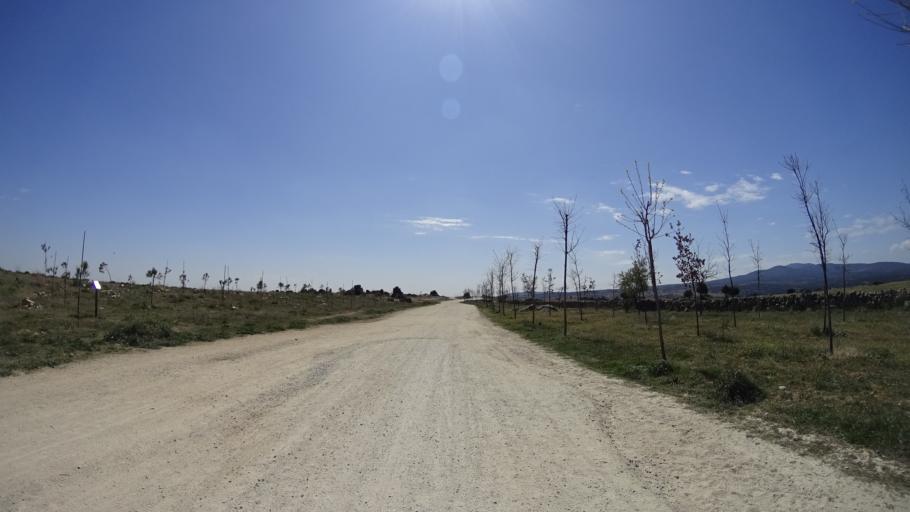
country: ES
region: Madrid
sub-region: Provincia de Madrid
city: Colmenar Viejo
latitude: 40.6626
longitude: -3.7876
